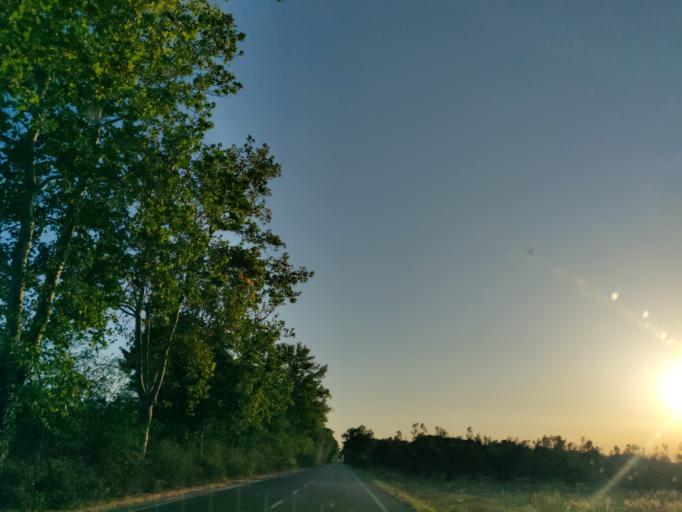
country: IT
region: Latium
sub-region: Provincia di Viterbo
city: Montalto di Castro
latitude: 42.3985
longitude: 11.6830
